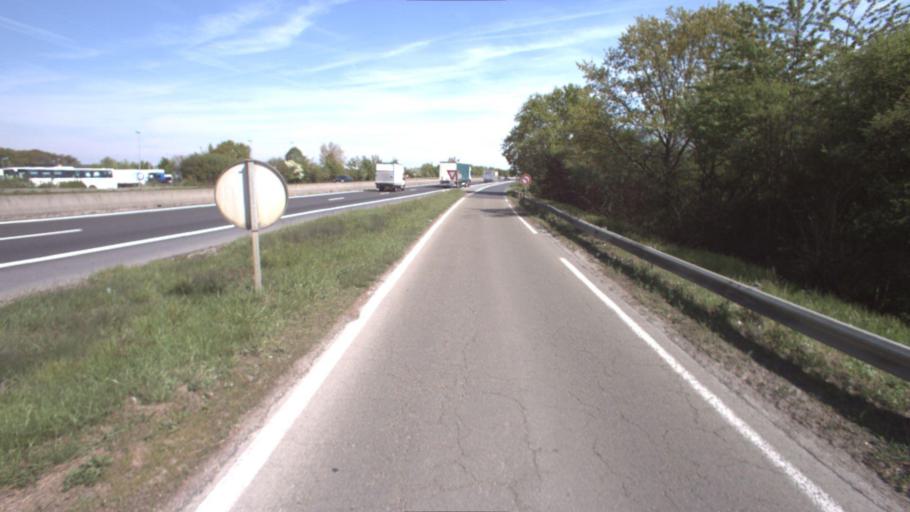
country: FR
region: Ile-de-France
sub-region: Departement de Seine-et-Marne
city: Saint-Mard
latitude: 49.0601
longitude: 2.7033
